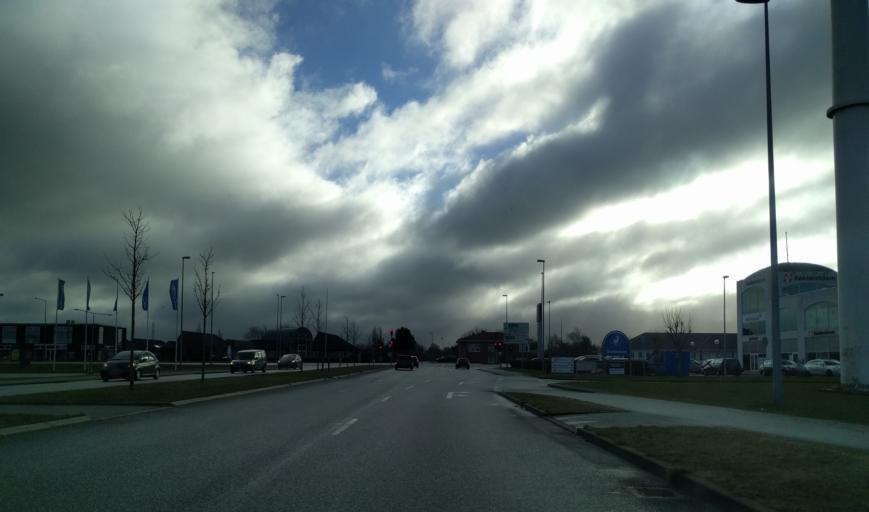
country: DK
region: North Denmark
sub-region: Alborg Kommune
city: Svenstrup
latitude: 57.0005
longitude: 9.8732
